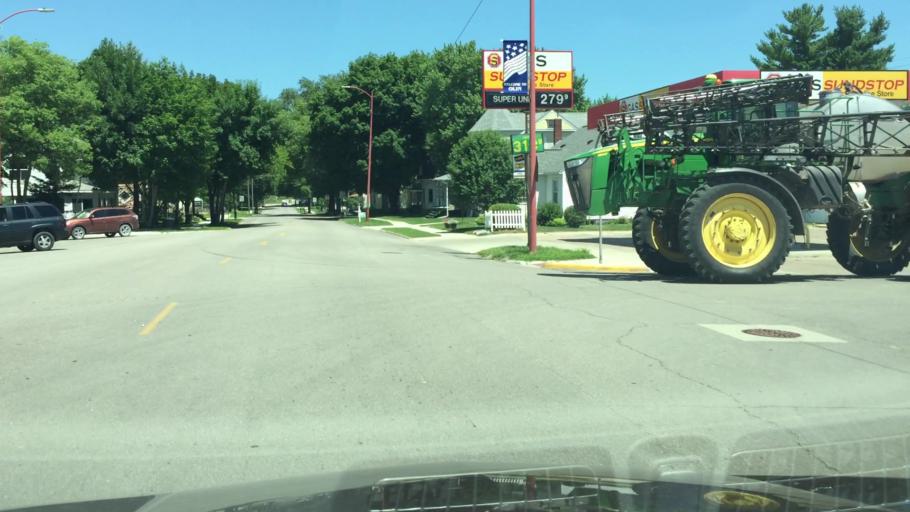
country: US
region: Iowa
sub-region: Cedar County
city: Mechanicsville
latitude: 41.9978
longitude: -91.1419
